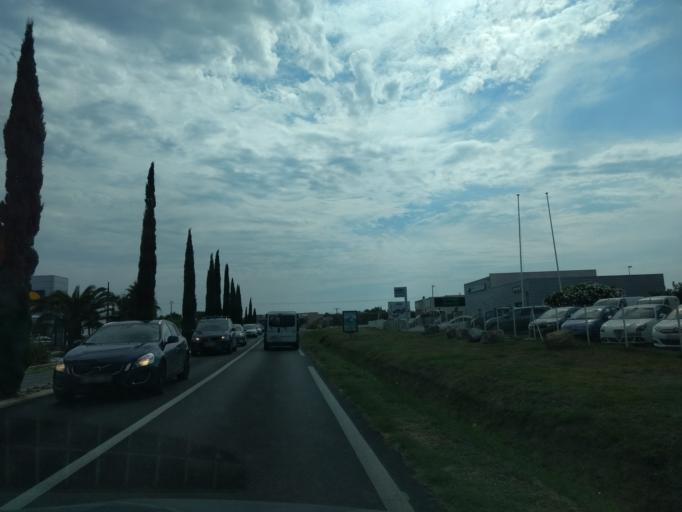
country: FR
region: Languedoc-Roussillon
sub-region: Departement des Pyrenees-Orientales
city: Saint-Laurent-de-la-Salanque
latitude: 42.7740
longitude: 3.0145
